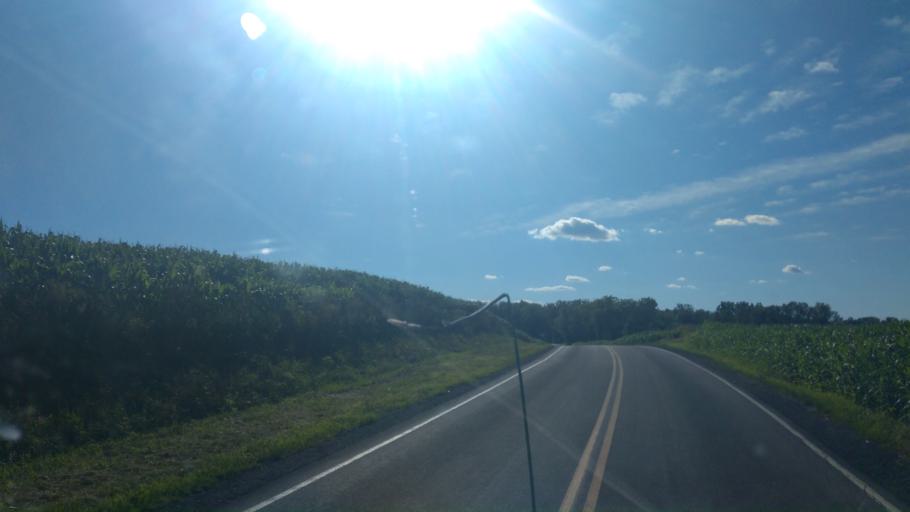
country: US
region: New York
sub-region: Wayne County
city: Lyons
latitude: 42.9974
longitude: -76.9440
